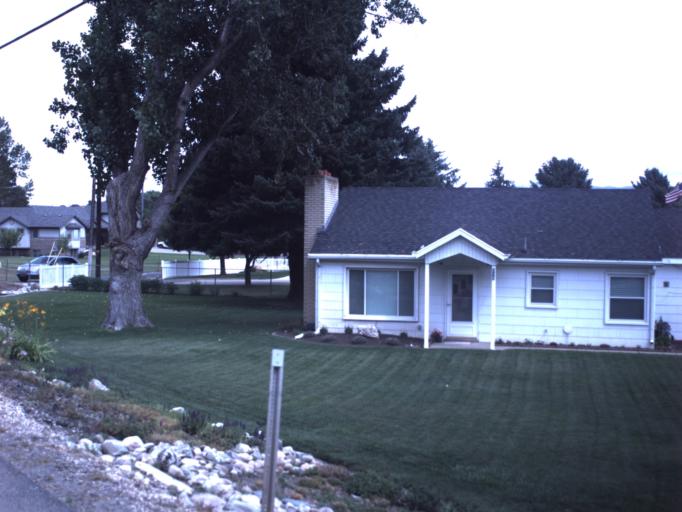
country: US
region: Utah
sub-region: Weber County
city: Washington Terrace
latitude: 41.1425
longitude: -111.9738
